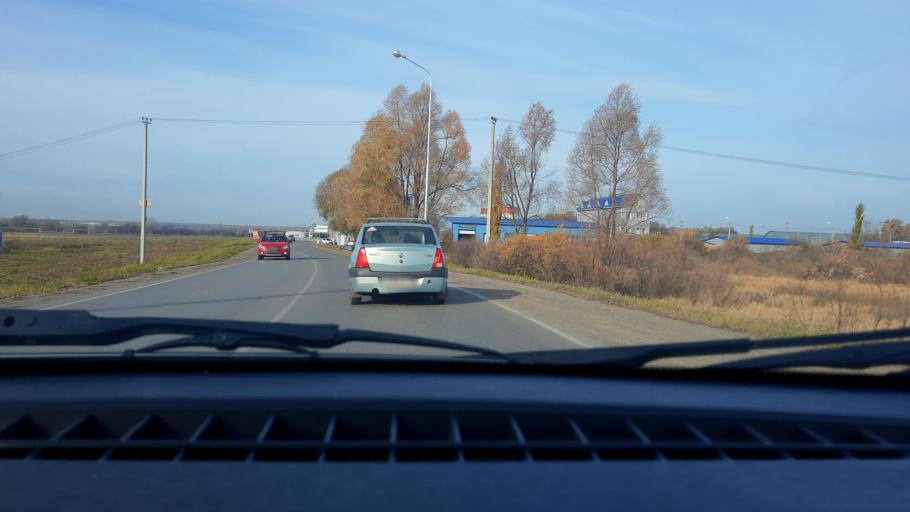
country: RU
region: Bashkortostan
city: Mikhaylovka
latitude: 54.7989
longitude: 55.8580
